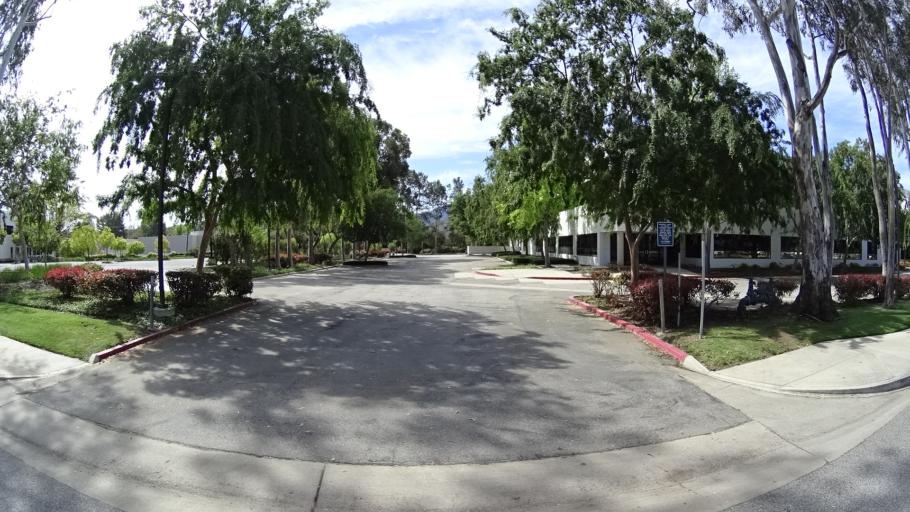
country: US
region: California
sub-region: Ventura County
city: Casa Conejo
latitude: 34.1967
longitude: -118.9261
